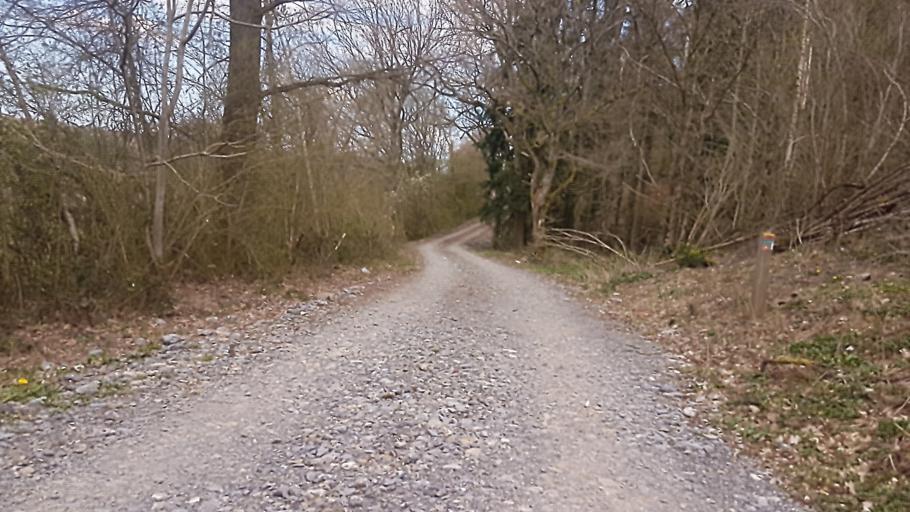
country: BE
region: Wallonia
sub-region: Province de Namur
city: Couvin
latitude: 50.0686
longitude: 4.5875
